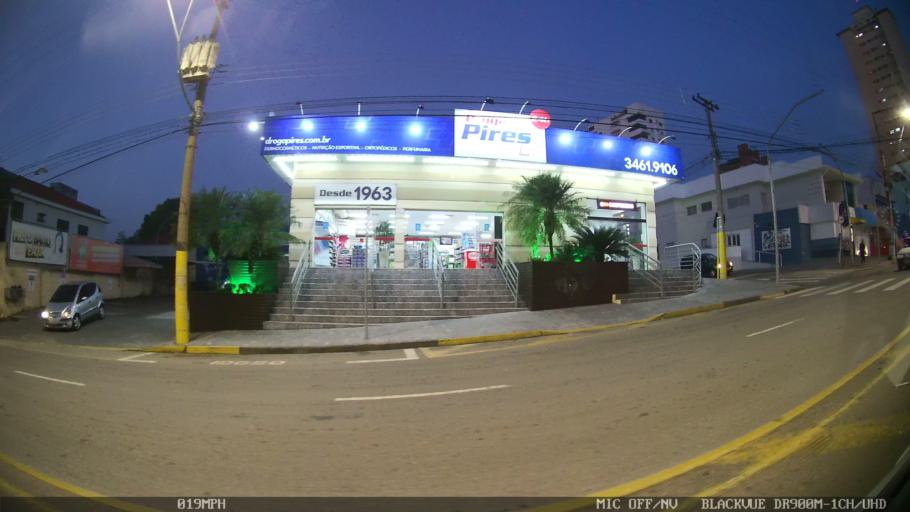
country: BR
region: Sao Paulo
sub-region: Americana
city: Americana
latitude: -22.7424
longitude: -47.3294
